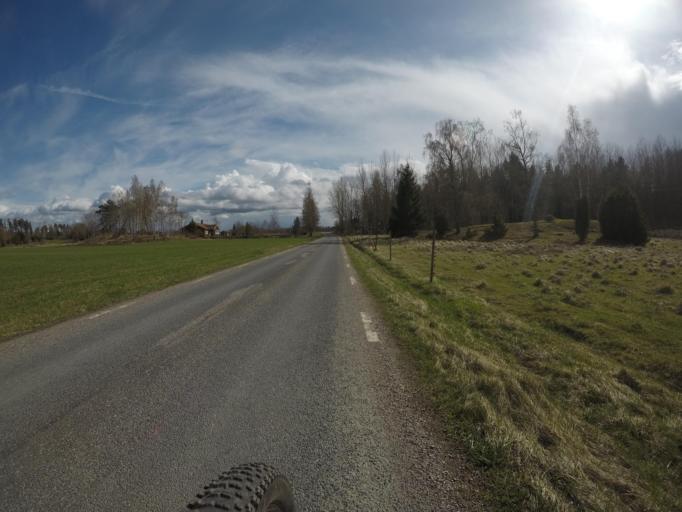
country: SE
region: Vaestmanland
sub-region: Kungsors Kommun
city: Kungsoer
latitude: 59.2958
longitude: 16.1417
